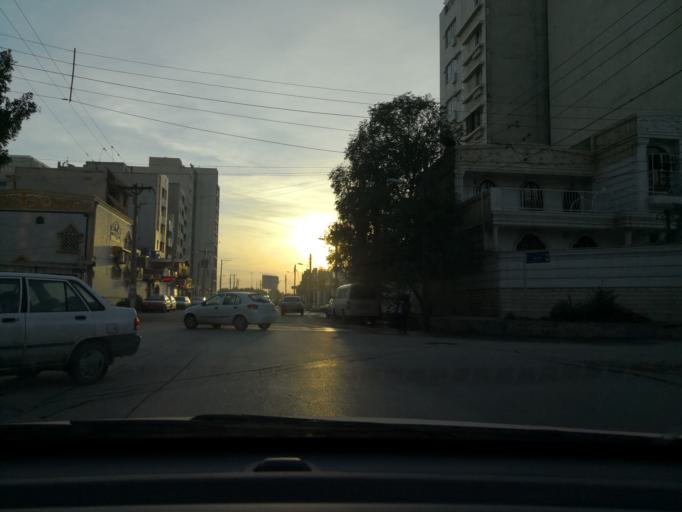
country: IR
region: Khuzestan
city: Ahvaz
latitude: 31.3487
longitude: 48.6926
